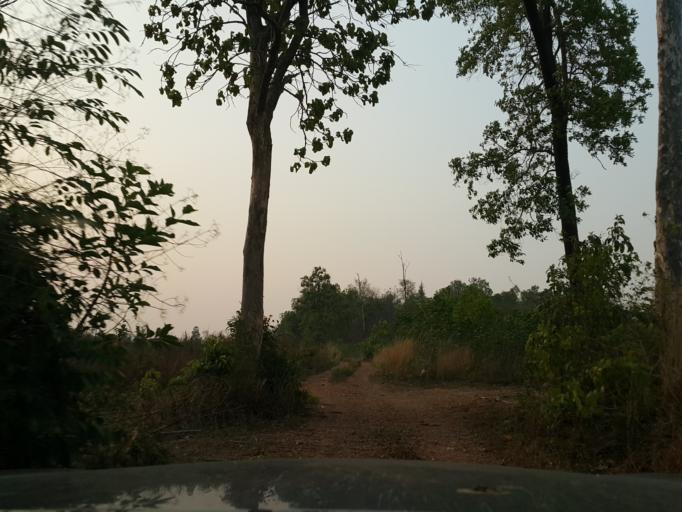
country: TH
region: Lamphun
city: Thung Hua Chang
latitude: 17.9135
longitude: 99.0742
